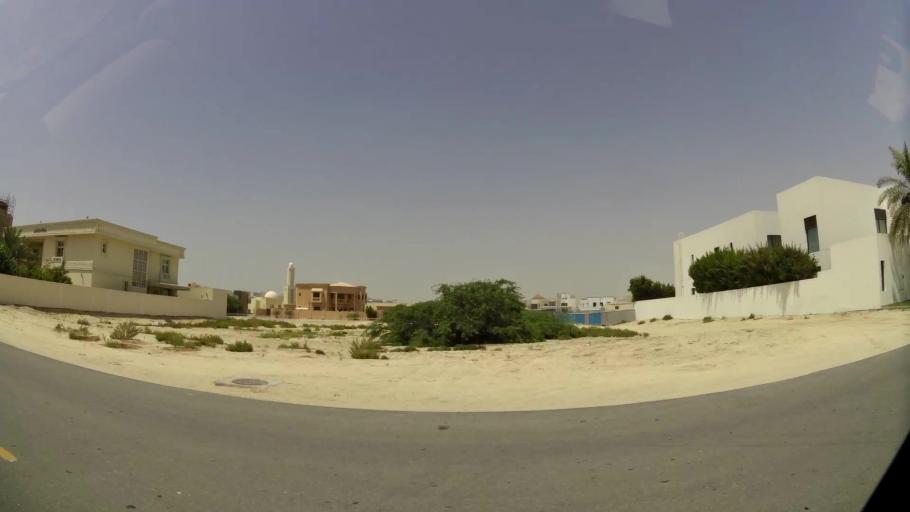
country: AE
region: Dubai
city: Dubai
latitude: 25.1348
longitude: 55.2033
